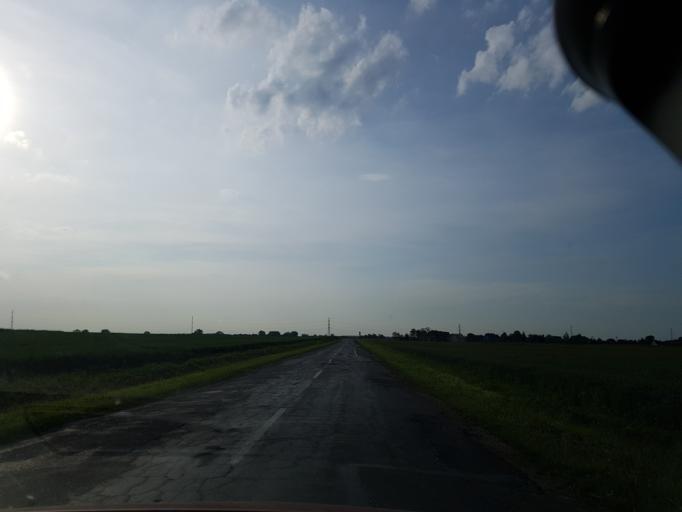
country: PL
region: Lower Silesian Voivodeship
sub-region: Powiat wroclawski
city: Gniechowice
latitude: 50.9691
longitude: 16.8690
